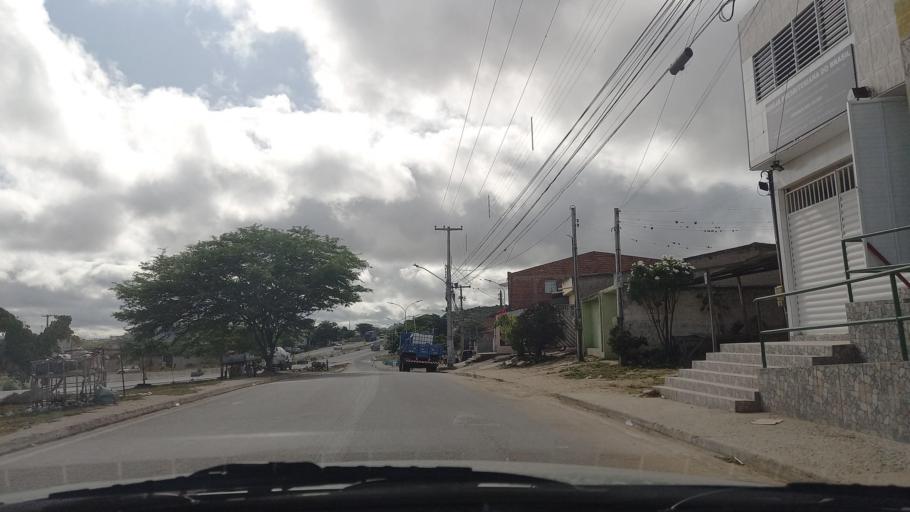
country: BR
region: Pernambuco
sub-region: Caruaru
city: Caruaru
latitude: -8.3017
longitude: -35.9987
